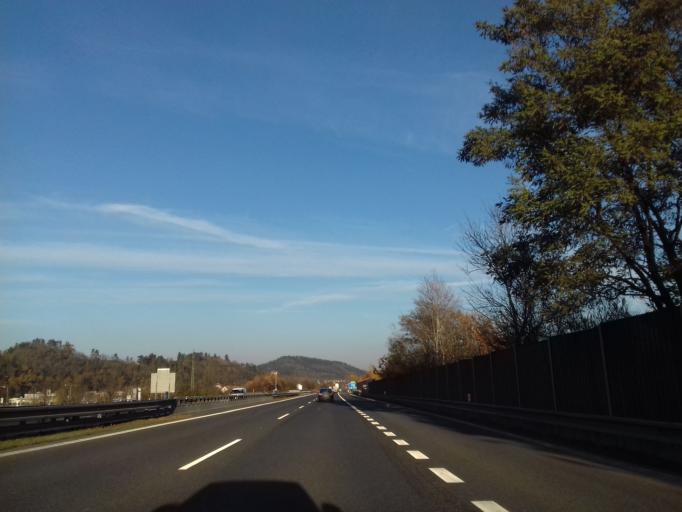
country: CZ
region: Central Bohemia
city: Zdice
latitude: 49.9006
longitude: 13.9595
